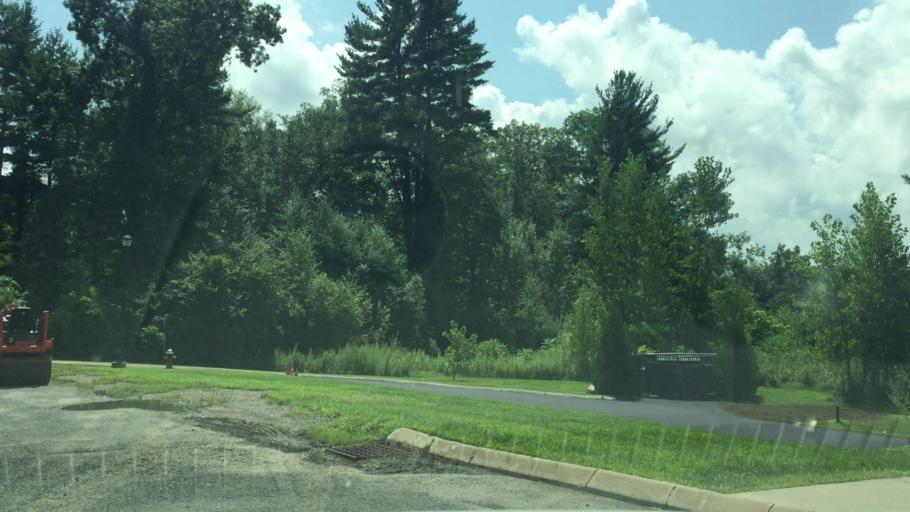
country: US
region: Massachusetts
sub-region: Berkshire County
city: Great Barrington
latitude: 42.2091
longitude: -73.3385
